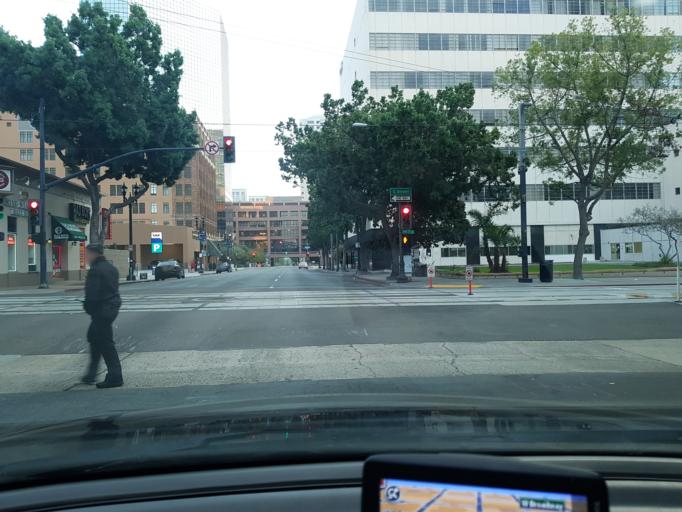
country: US
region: California
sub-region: San Diego County
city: San Diego
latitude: 32.7169
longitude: -117.1648
